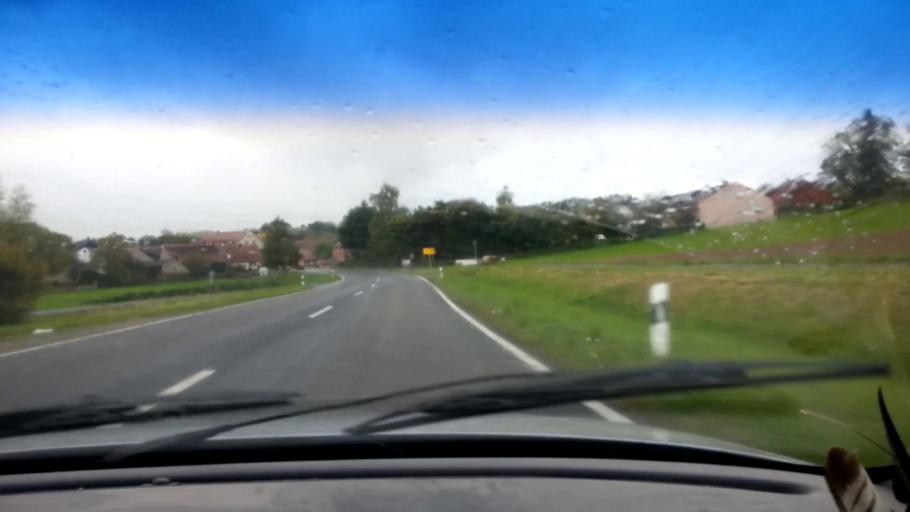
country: DE
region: Bavaria
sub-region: Upper Franconia
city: Walsdorf
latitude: 49.8721
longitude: 10.8032
